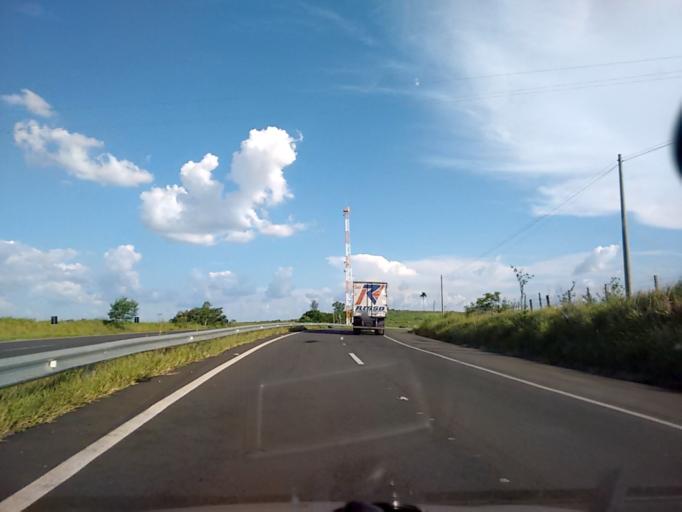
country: BR
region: Sao Paulo
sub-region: Duartina
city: Duartina
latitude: -22.2839
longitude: -49.4925
